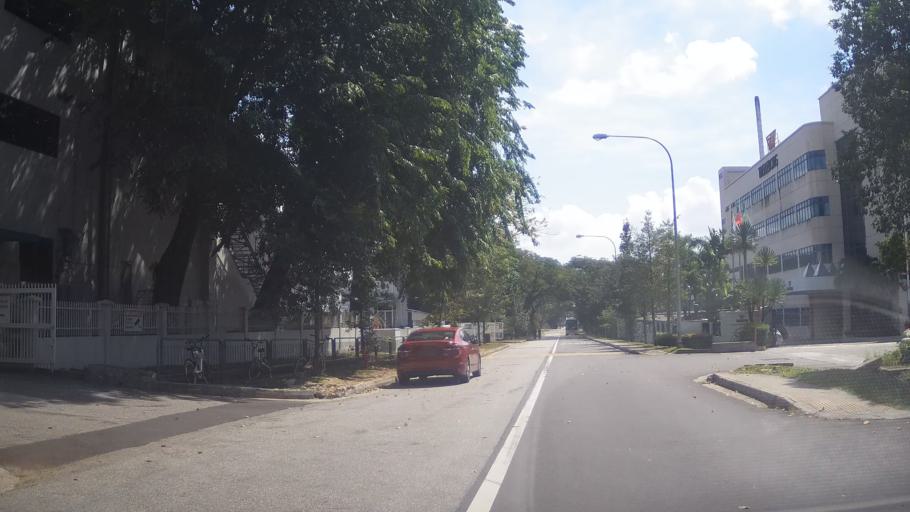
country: SG
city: Singapore
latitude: 1.3201
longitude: 103.7129
